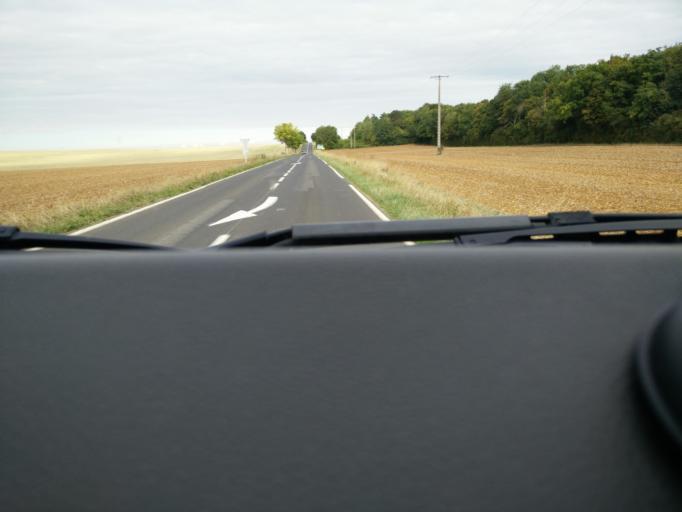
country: FR
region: Lorraine
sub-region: Departement de Meurthe-et-Moselle
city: Montauville
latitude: 48.8946
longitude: 5.9771
